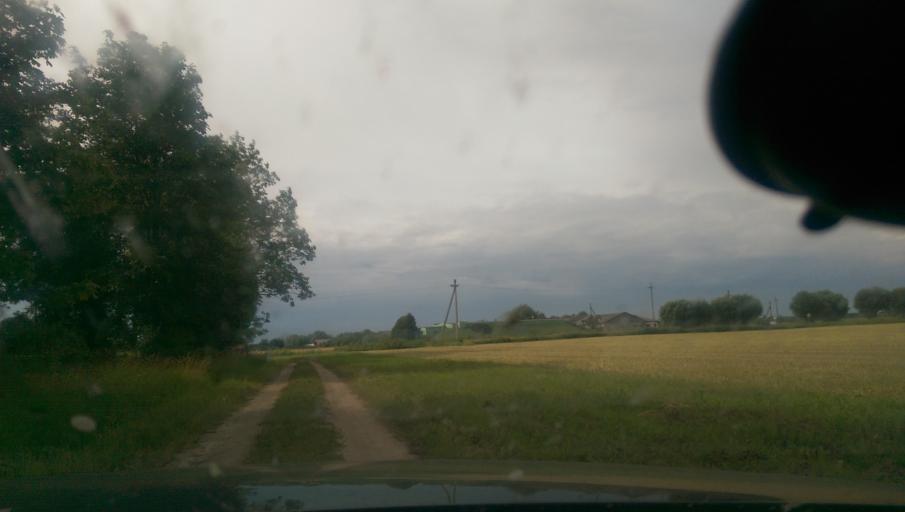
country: LT
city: Rusne
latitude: 55.2933
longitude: 21.3686
